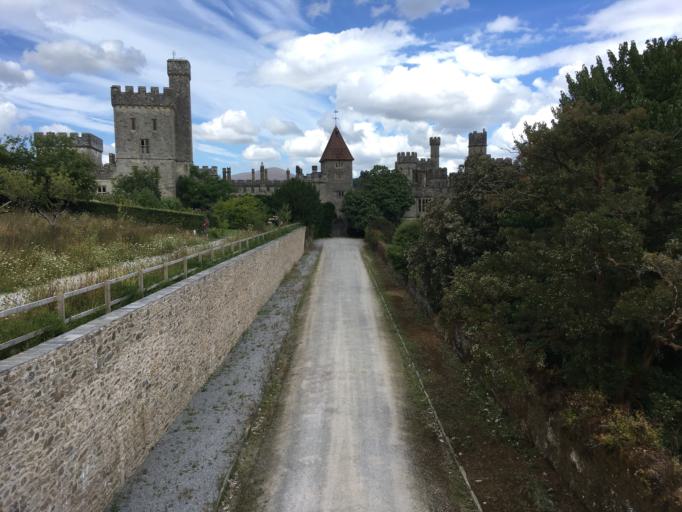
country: IE
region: Munster
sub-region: County Cork
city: Youghal
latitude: 52.1395
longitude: -7.9325
